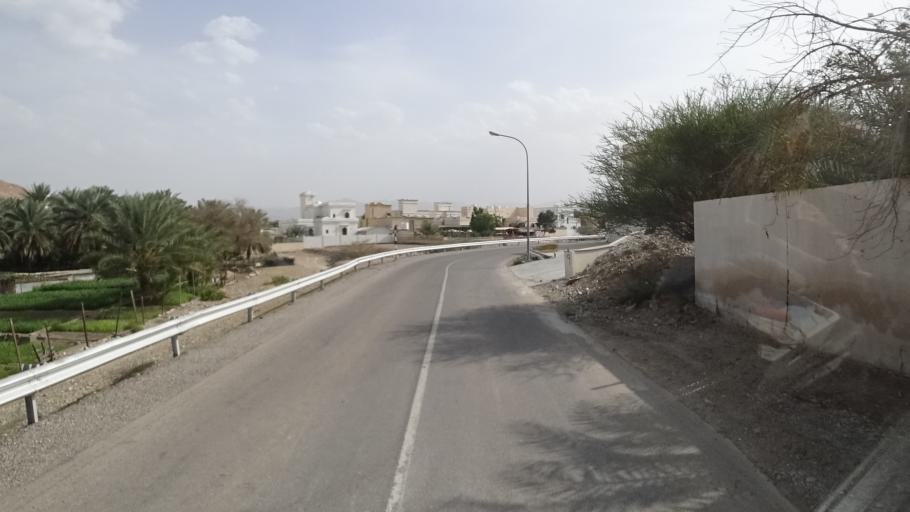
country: OM
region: Muhafazat Masqat
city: Bawshar
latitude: 23.3891
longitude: 58.5175
